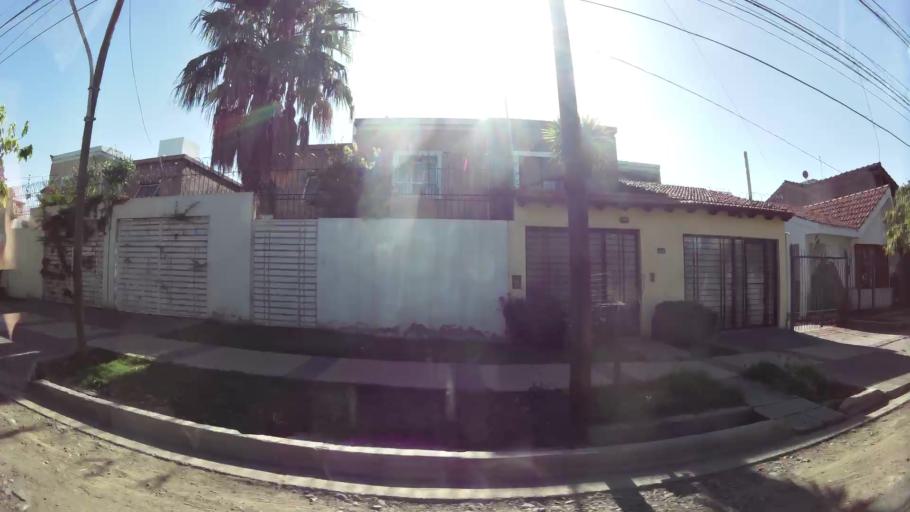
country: AR
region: Mendoza
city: Mendoza
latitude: -32.9057
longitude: -68.8184
